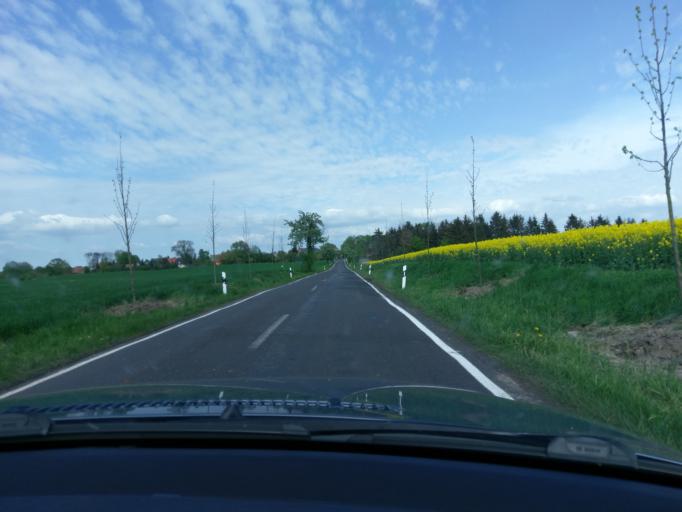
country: DE
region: Brandenburg
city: Hohenfinow
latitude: 52.7544
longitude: 13.8720
